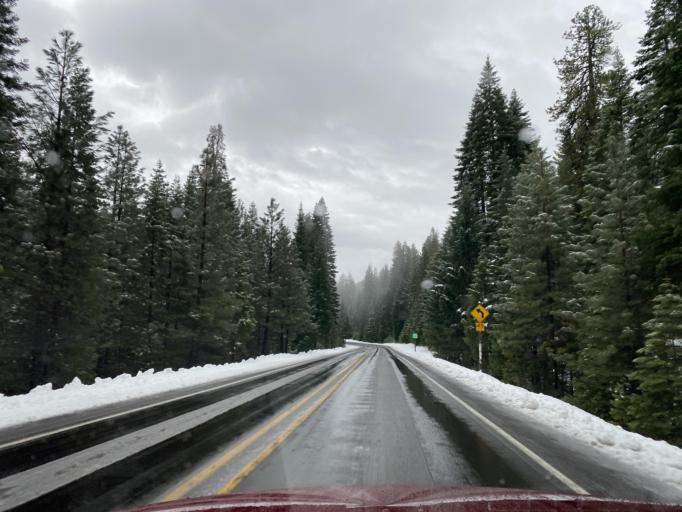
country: US
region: Oregon
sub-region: Klamath County
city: Klamath Falls
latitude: 42.5284
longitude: -122.0893
